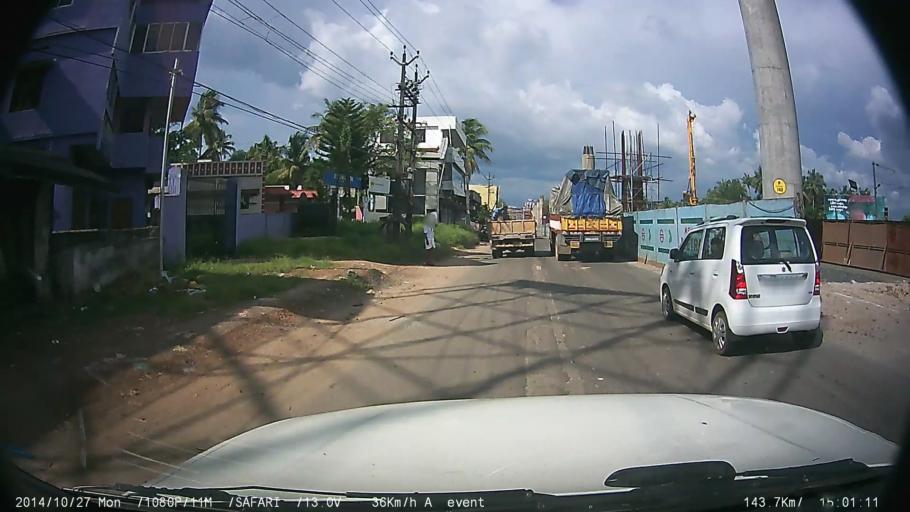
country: IN
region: Kerala
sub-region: Ernakulam
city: Aluva
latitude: 10.0780
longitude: 76.3383
